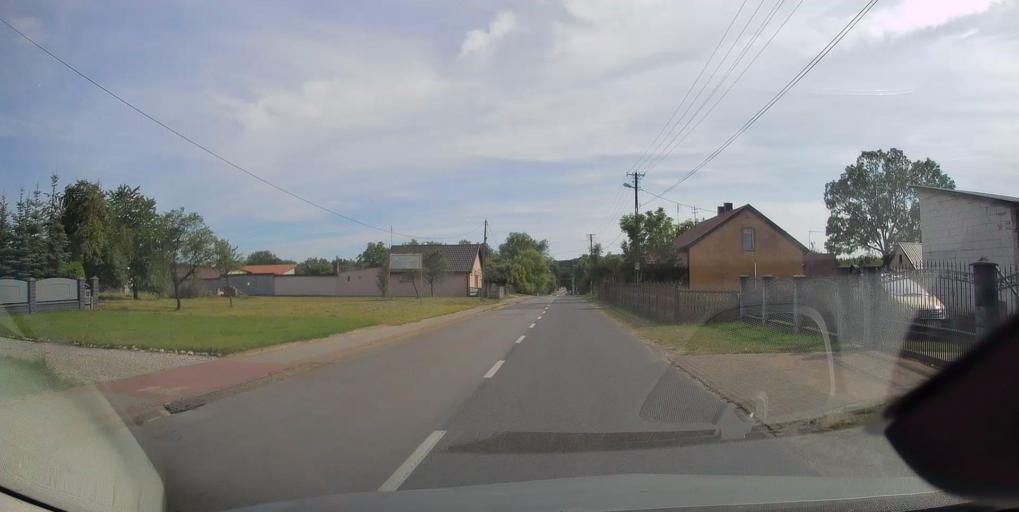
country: PL
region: Lodz Voivodeship
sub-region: Powiat tomaszowski
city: Tomaszow Mazowiecki
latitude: 51.4884
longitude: 19.9888
